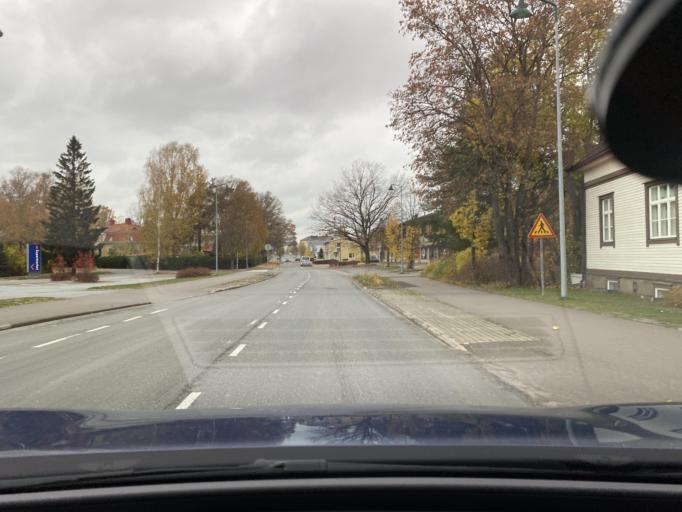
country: FI
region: Varsinais-Suomi
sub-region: Vakka-Suomi
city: Laitila
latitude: 60.8770
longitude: 21.6988
